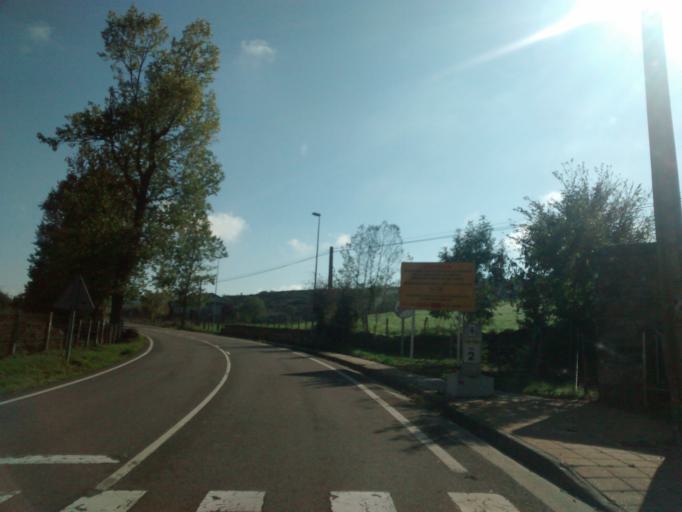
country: ES
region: Cantabria
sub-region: Provincia de Cantabria
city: Reinosa
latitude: 42.9898
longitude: -4.1237
